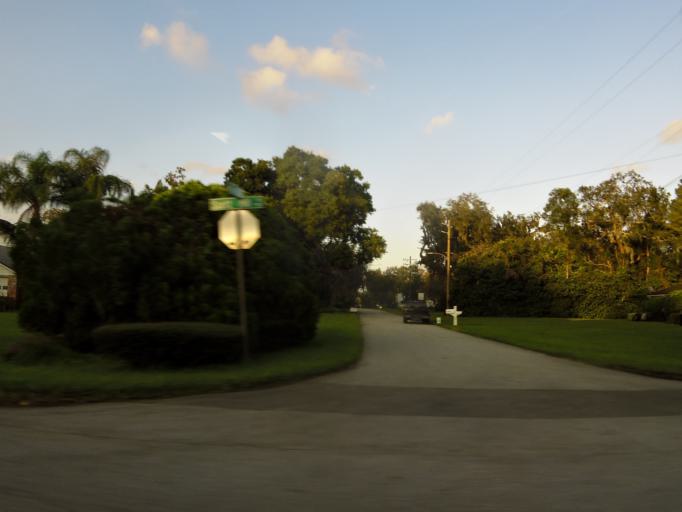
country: US
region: Florida
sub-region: Clay County
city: Orange Park
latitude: 30.1988
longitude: -81.6337
